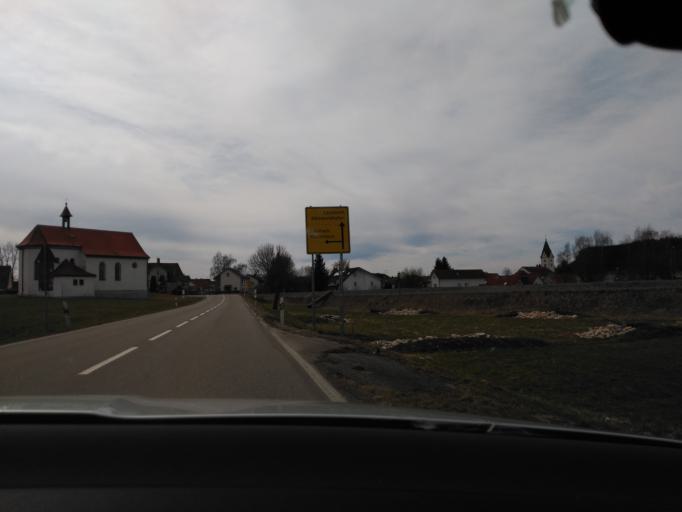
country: DE
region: Baden-Wuerttemberg
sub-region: Tuebingen Region
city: Aichstetten
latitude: 47.8969
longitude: 10.0858
